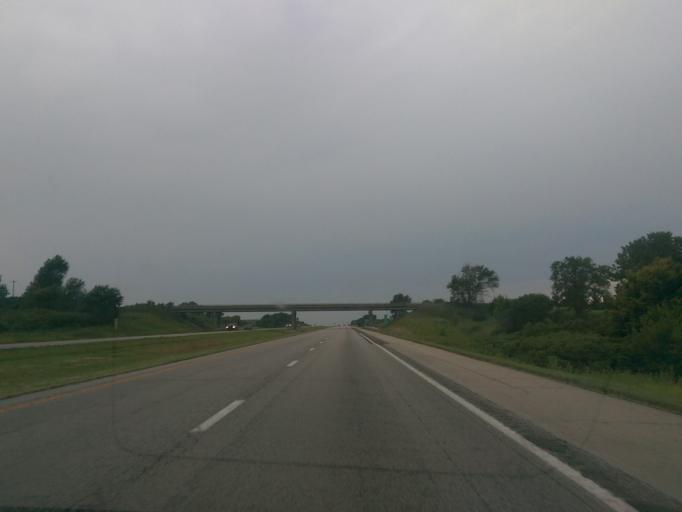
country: US
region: Missouri
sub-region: Holt County
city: Oregon
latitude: 40.0259
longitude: -95.1038
